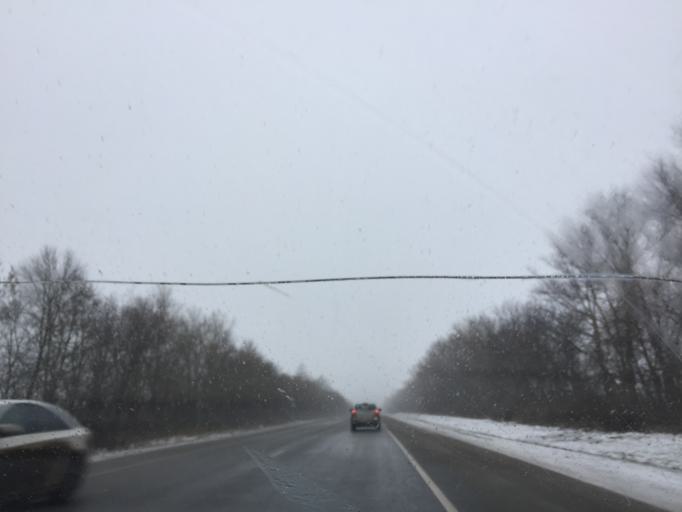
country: RU
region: Tula
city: Plavsk
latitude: 53.8008
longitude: 37.3799
